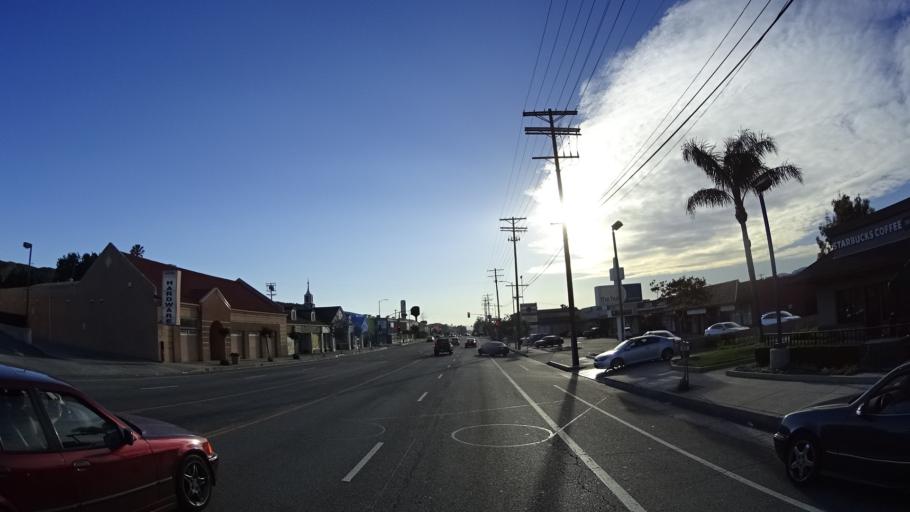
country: US
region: California
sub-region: Los Angeles County
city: Burbank
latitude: 34.2598
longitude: -118.3129
